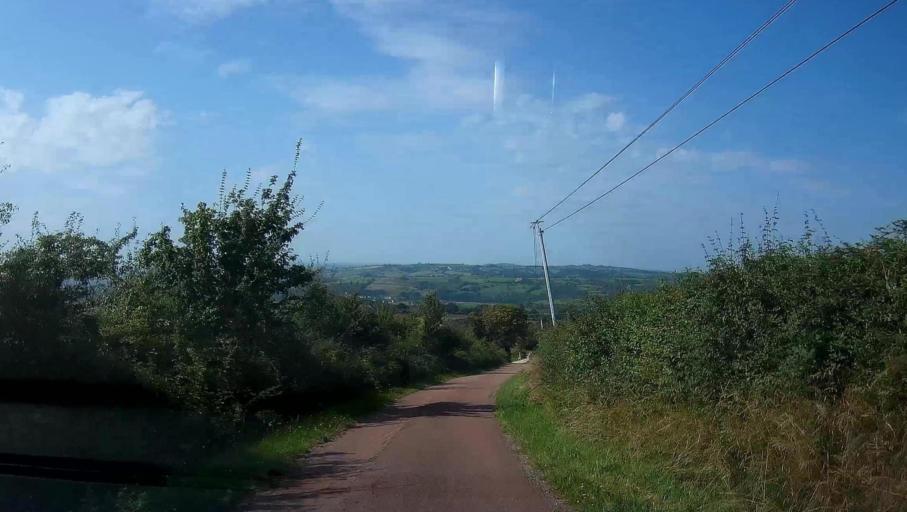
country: FR
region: Bourgogne
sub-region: Departement de la Cote-d'Or
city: Nolay
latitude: 46.9007
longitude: 4.6142
